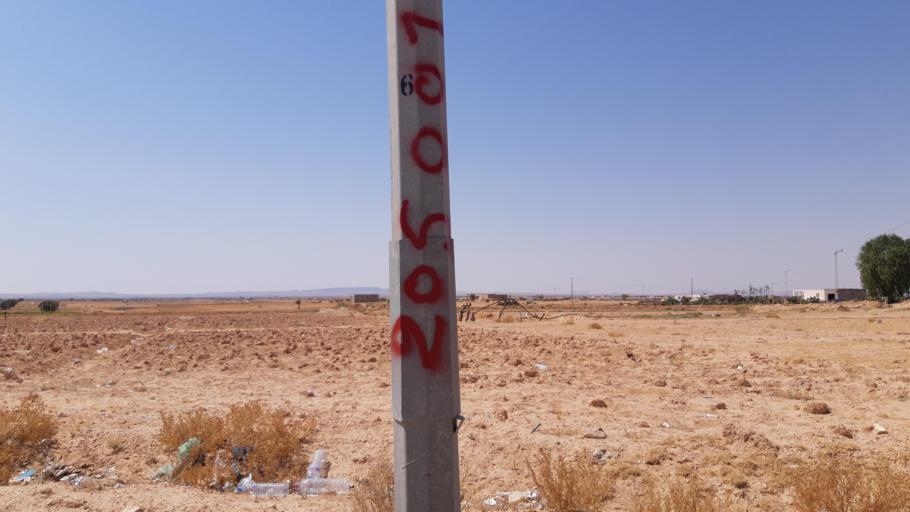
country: TN
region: Safaqis
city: Skhira
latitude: 34.2618
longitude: 9.8401
